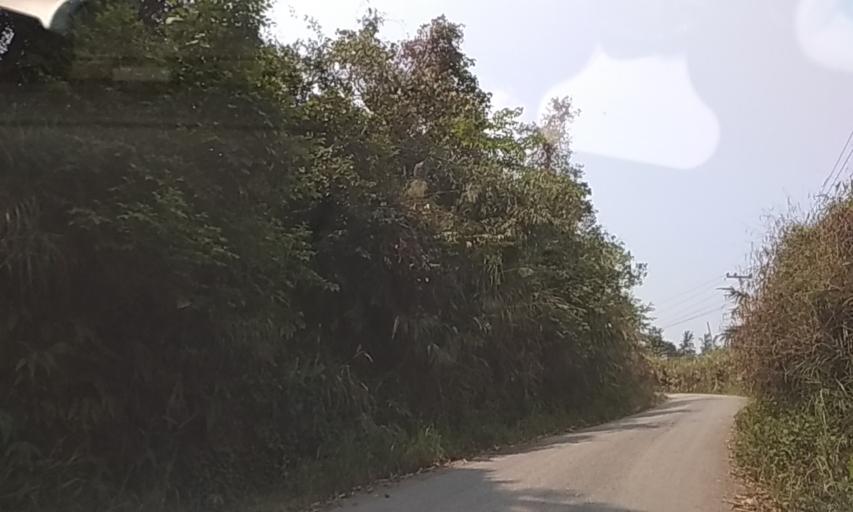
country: TH
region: Nan
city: Chaloem Phra Kiat
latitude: 20.0539
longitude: 101.0772
